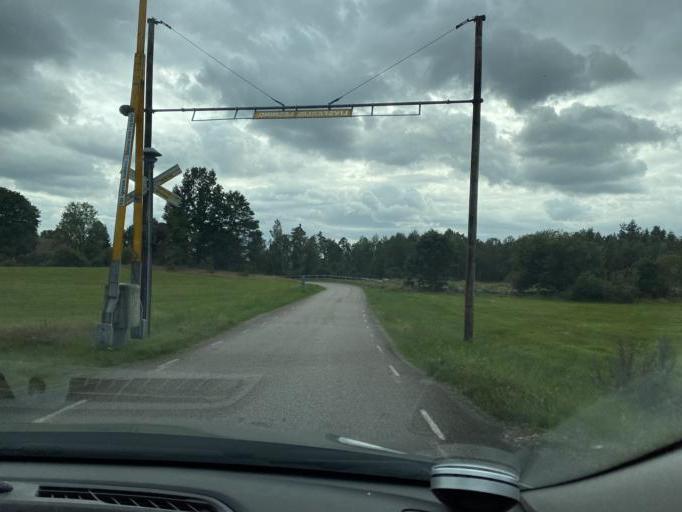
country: SE
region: Kronoberg
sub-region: Markaryds Kommun
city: Markaryd
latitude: 56.4771
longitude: 13.5654
